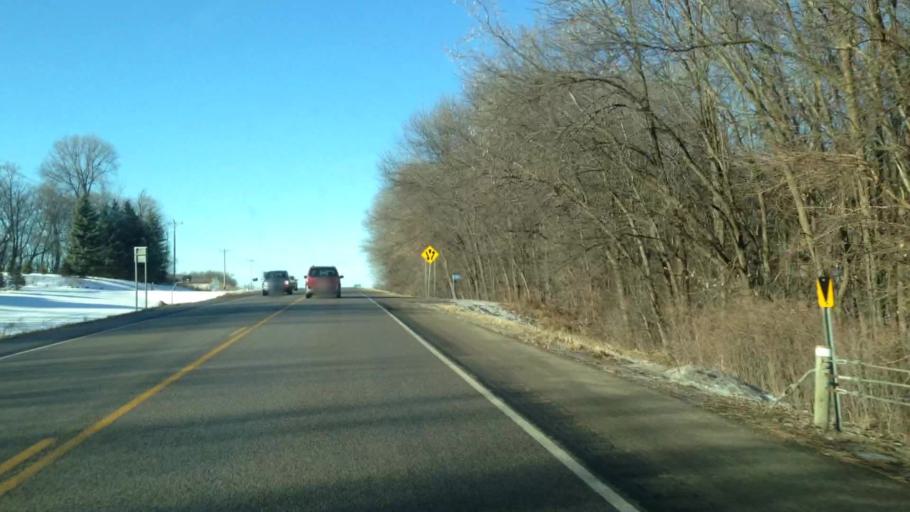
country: US
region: Minnesota
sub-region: Le Sueur County
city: New Prague
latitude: 44.5438
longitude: -93.4940
